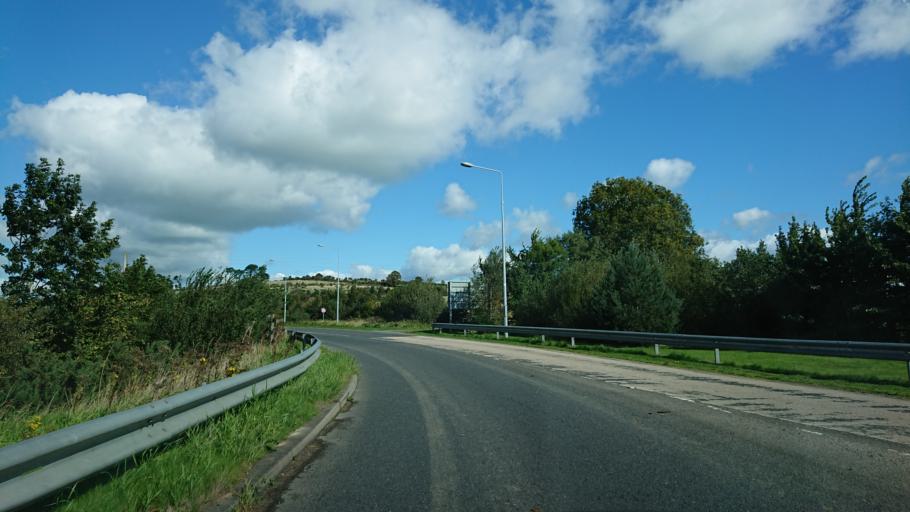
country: IE
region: Leinster
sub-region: Kilkenny
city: Mooncoin
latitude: 52.2370
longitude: -7.2471
